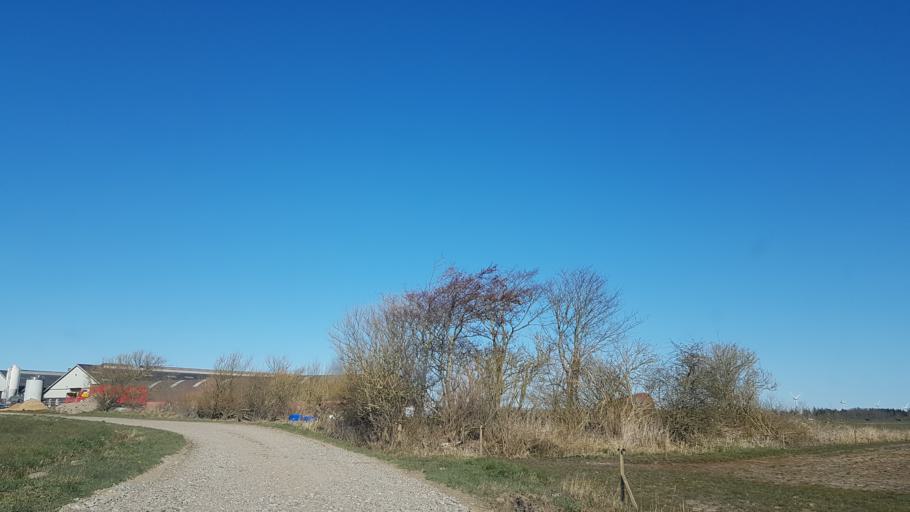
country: DK
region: South Denmark
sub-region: Tonder Kommune
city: Sherrebek
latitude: 55.2418
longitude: 8.7132
